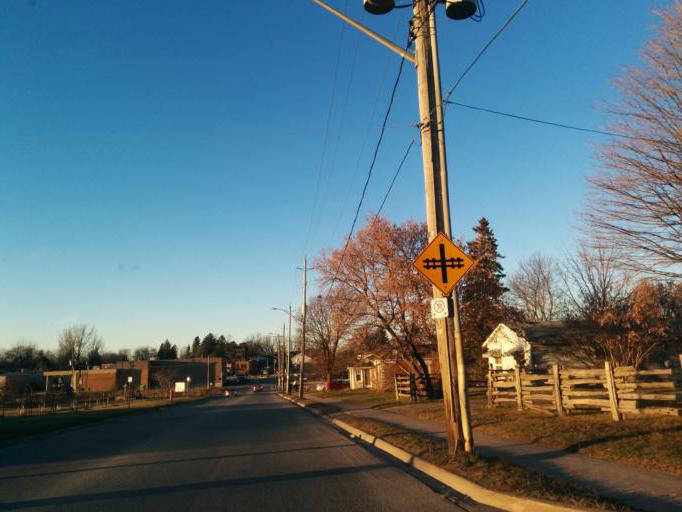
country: CA
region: Ontario
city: Orangeville
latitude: 43.9157
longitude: -80.1033
